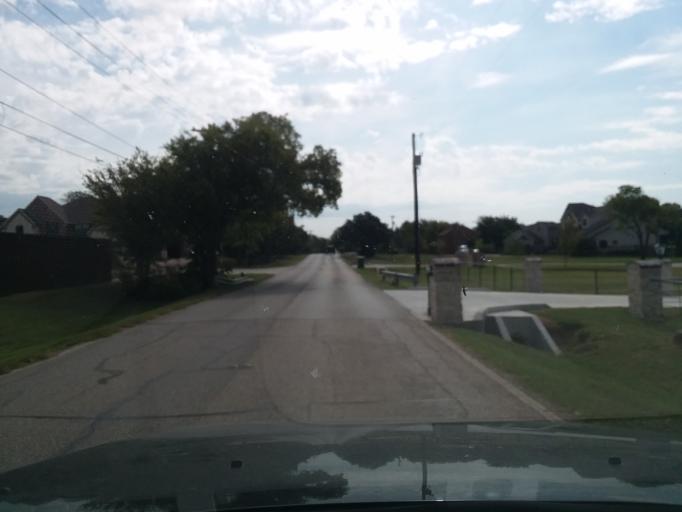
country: US
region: Texas
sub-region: Denton County
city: Double Oak
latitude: 33.0584
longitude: -97.1130
